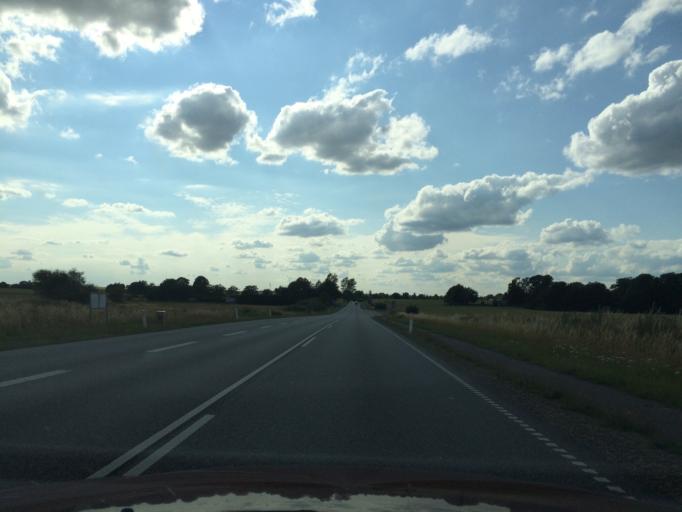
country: DK
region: Central Jutland
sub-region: Favrskov Kommune
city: Hammel
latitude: 56.2370
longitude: 9.8282
